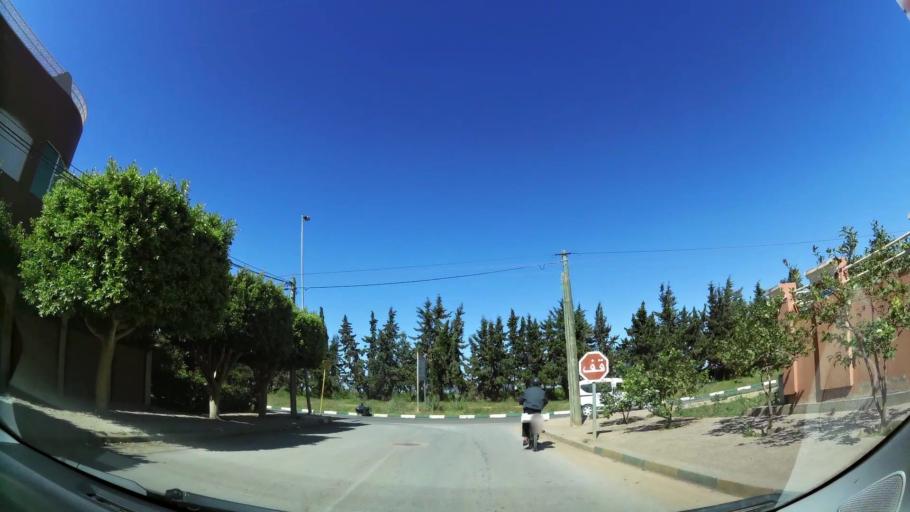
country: MA
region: Oriental
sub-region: Berkane-Taourirt
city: Berkane
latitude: 34.9461
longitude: -2.3272
